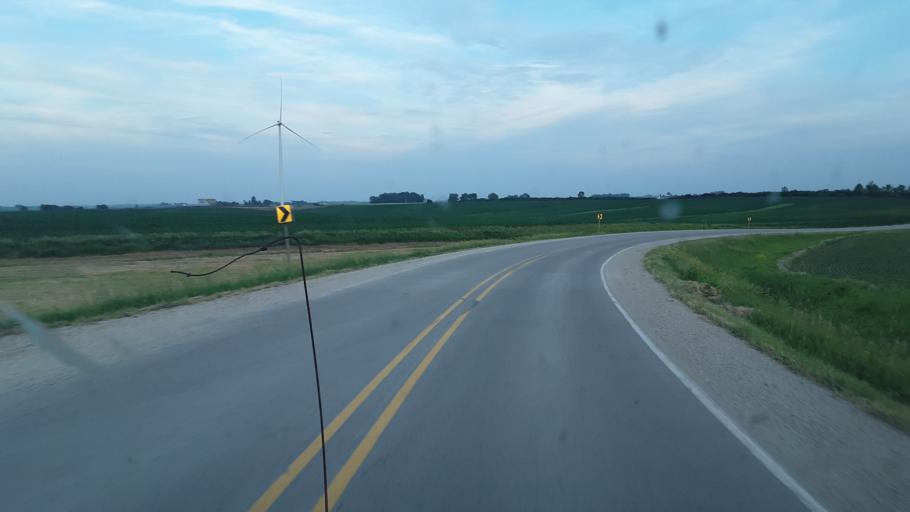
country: US
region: Iowa
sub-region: Iowa County
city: Marengo
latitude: 41.7020
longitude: -92.1632
